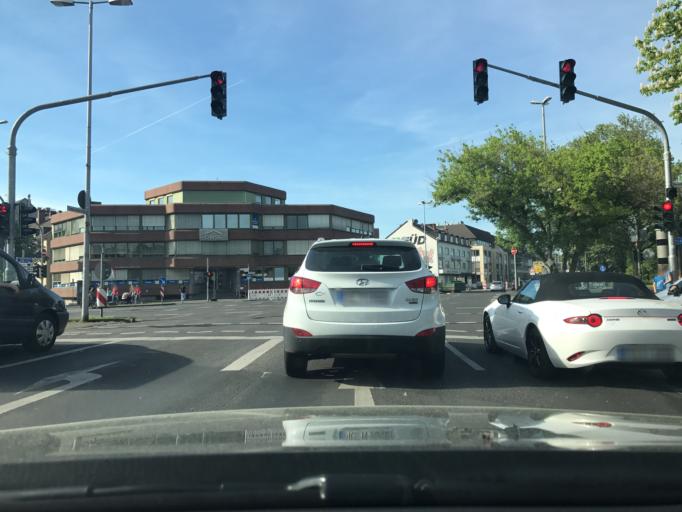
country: DE
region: North Rhine-Westphalia
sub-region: Regierungsbezirk Dusseldorf
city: Monchengladbach
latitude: 51.1908
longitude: 6.4422
